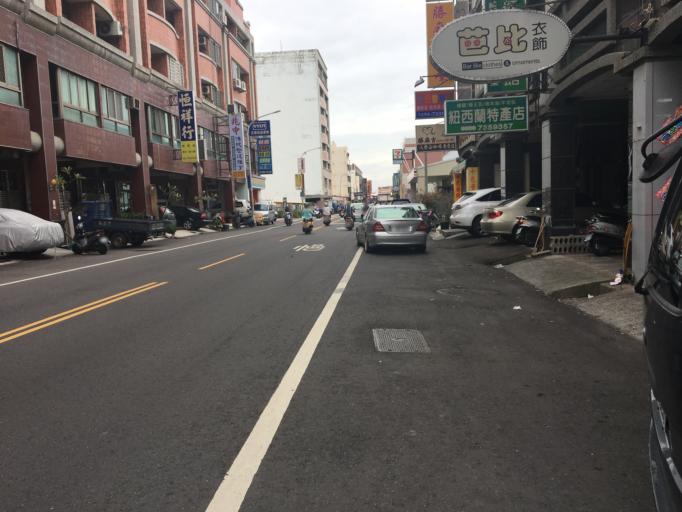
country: TW
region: Taiwan
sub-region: Changhua
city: Chang-hua
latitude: 24.0917
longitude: 120.5429
